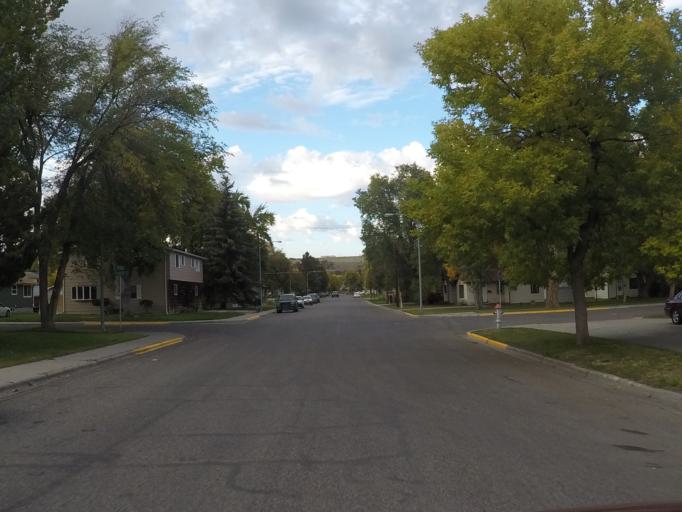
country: US
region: Montana
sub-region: Yellowstone County
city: Billings
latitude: 45.7877
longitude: -108.5306
